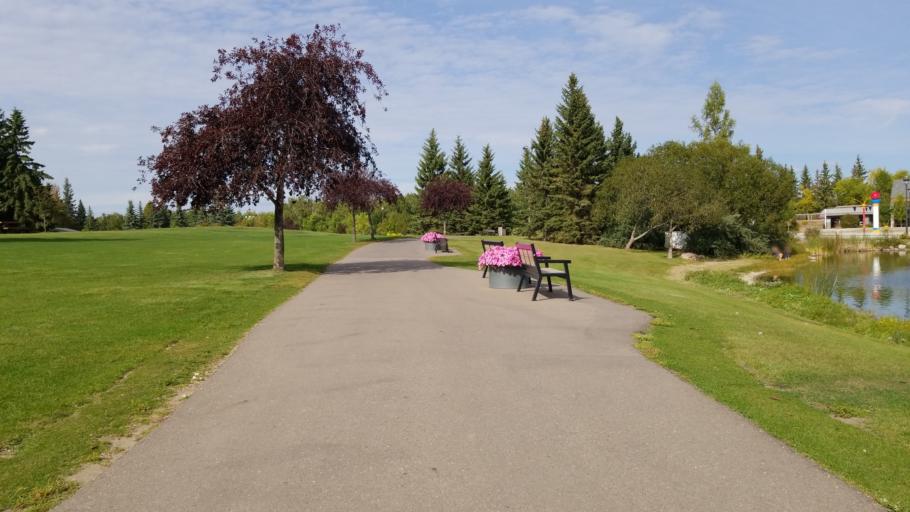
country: CA
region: Saskatchewan
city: Lloydminster
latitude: 53.2605
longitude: -110.0404
